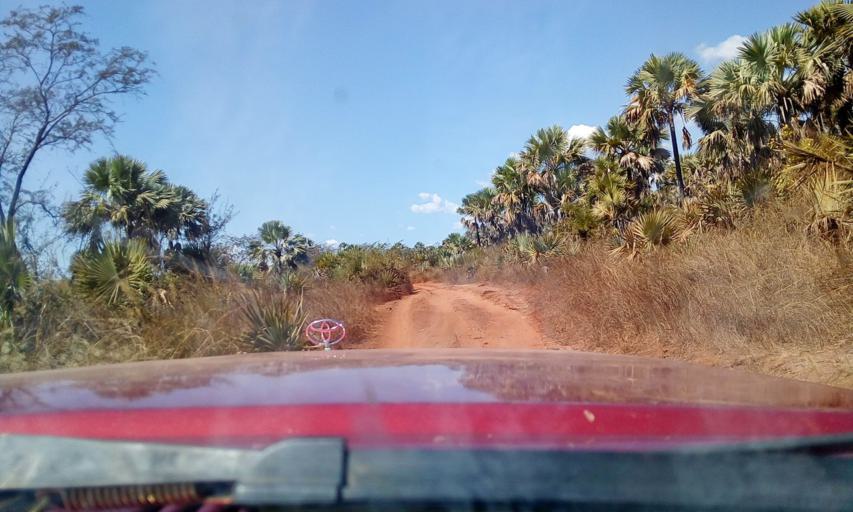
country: MG
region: Boeny
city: Sitampiky
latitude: -16.1220
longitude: 45.4211
